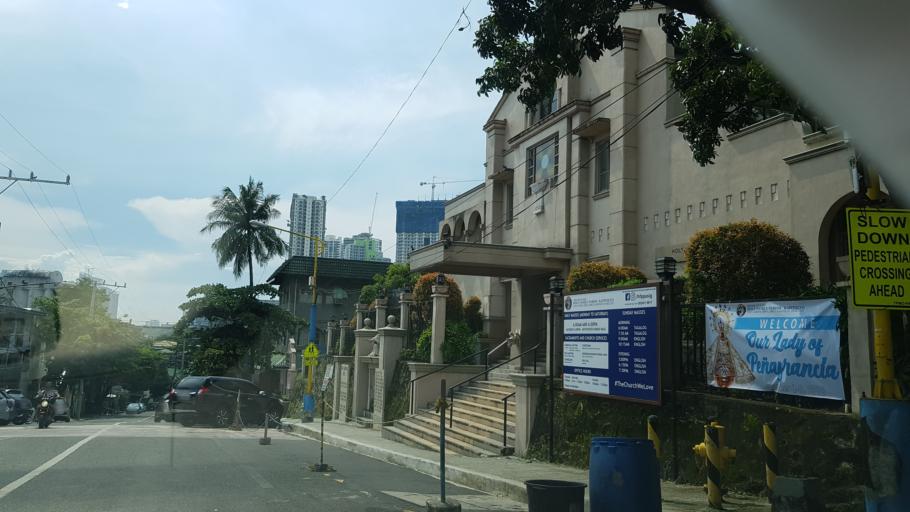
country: PH
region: Metro Manila
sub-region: Pasig
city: Pasig City
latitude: 14.5676
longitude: 121.0578
